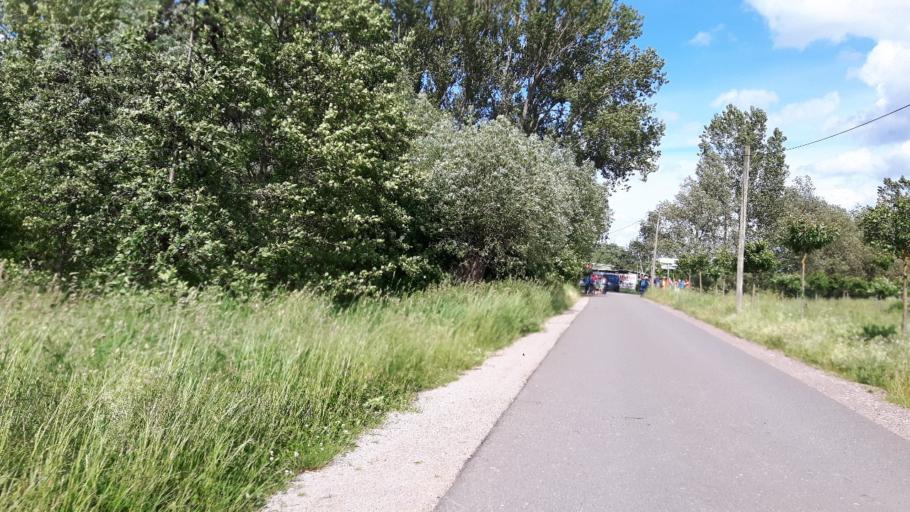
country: DE
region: Thuringia
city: Stadtilm
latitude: 50.7802
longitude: 11.0967
